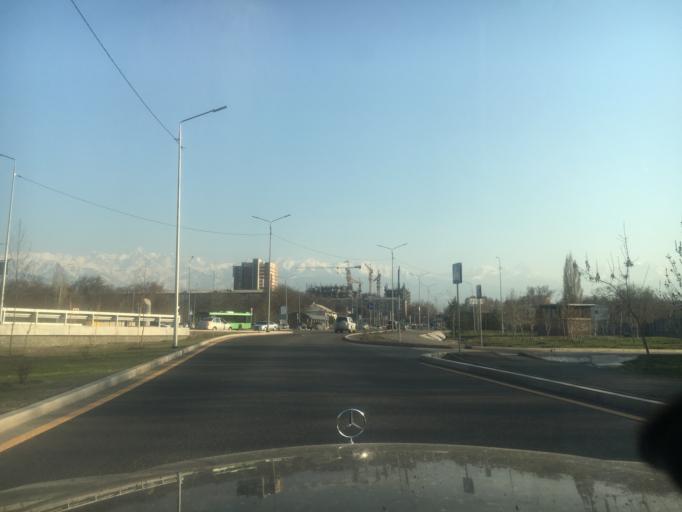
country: KZ
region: Almaty Qalasy
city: Almaty
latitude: 43.2737
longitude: 76.9443
